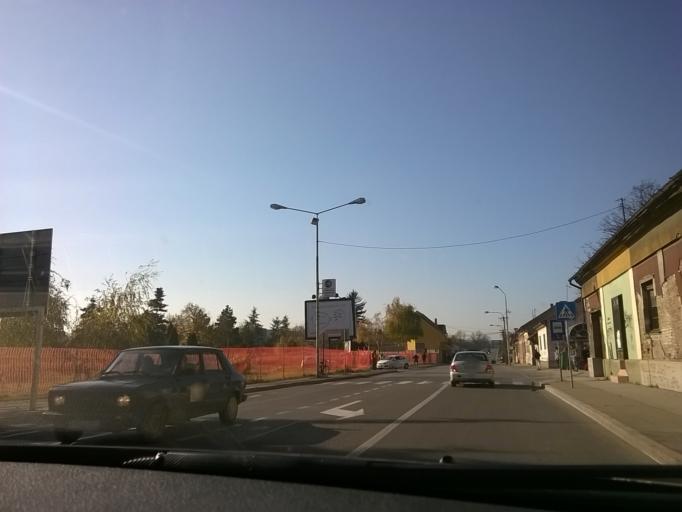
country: RS
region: Autonomna Pokrajina Vojvodina
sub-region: Juznobanatski Okrug
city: Pancevo
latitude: 44.8737
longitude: 20.6366
